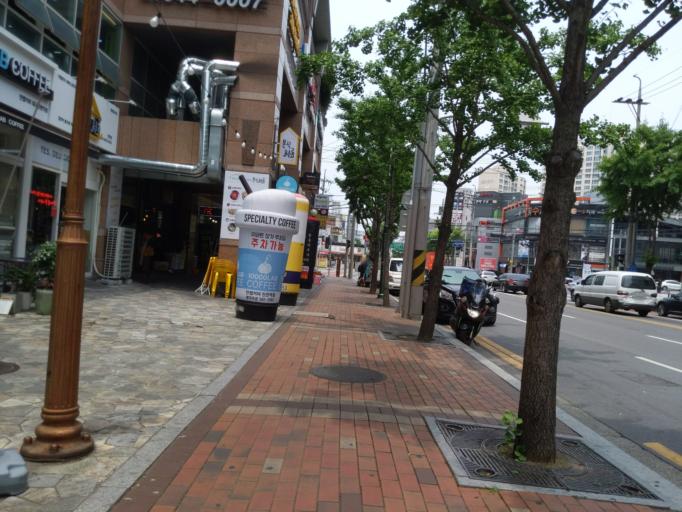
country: KR
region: Daegu
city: Hwawon
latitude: 35.8136
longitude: 128.5242
